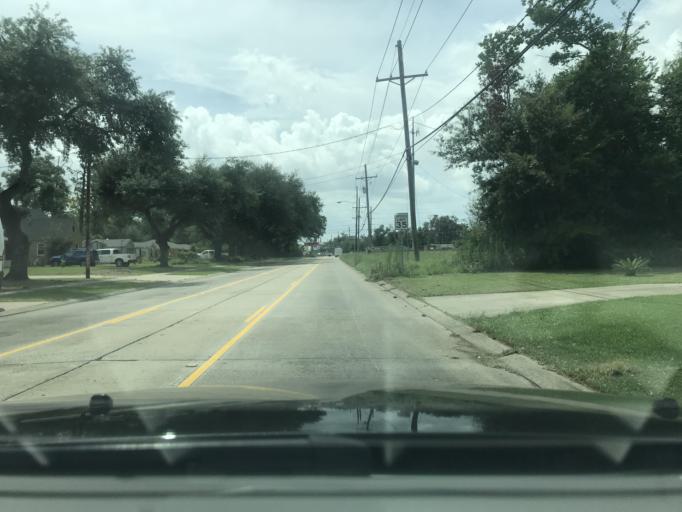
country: US
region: Louisiana
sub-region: Calcasieu Parish
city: Lake Charles
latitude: 30.2131
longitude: -93.1994
